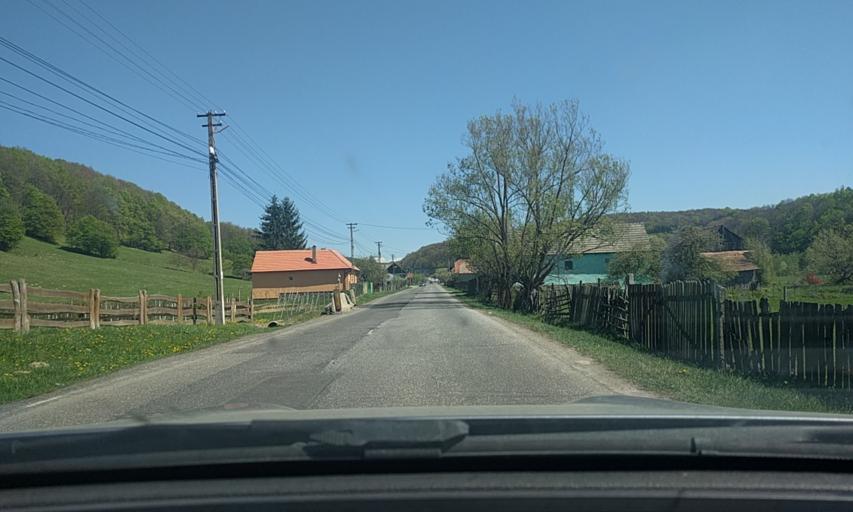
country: RO
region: Covasna
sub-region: Comuna Dobarlau
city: Dobarlau
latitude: 45.6820
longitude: 25.9159
